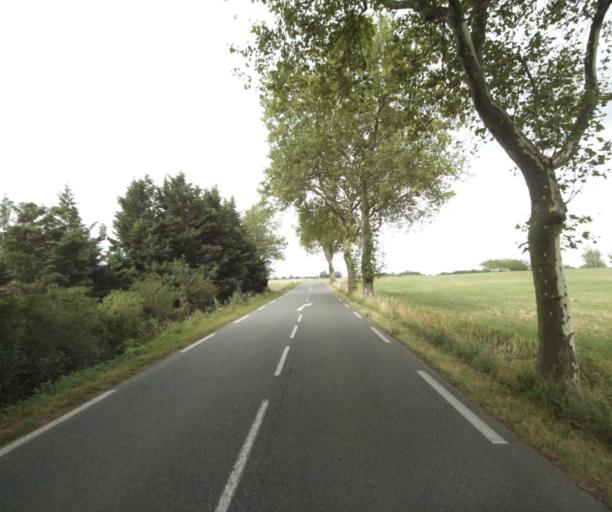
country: FR
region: Midi-Pyrenees
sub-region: Departement du Tarn
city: Soreze
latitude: 43.4617
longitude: 2.0796
